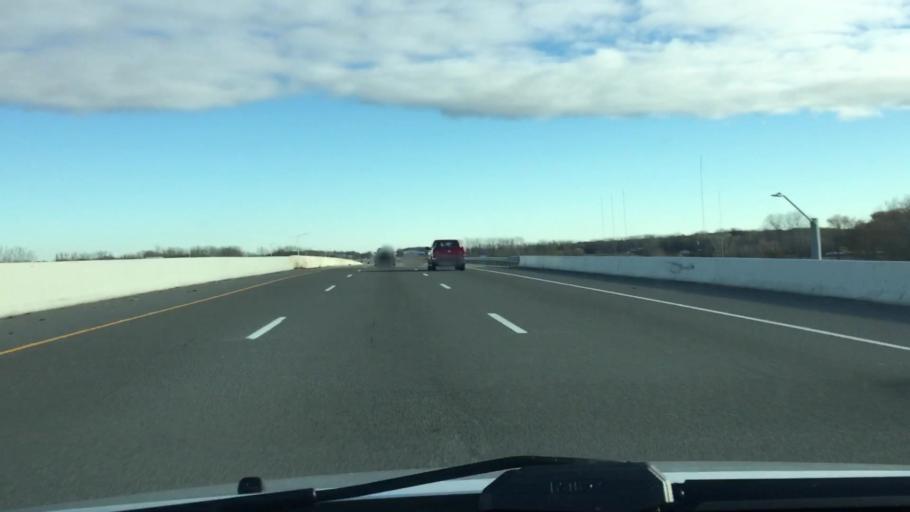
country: US
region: Wisconsin
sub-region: Winnebago County
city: Oshkosh
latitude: 44.0965
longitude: -88.5435
